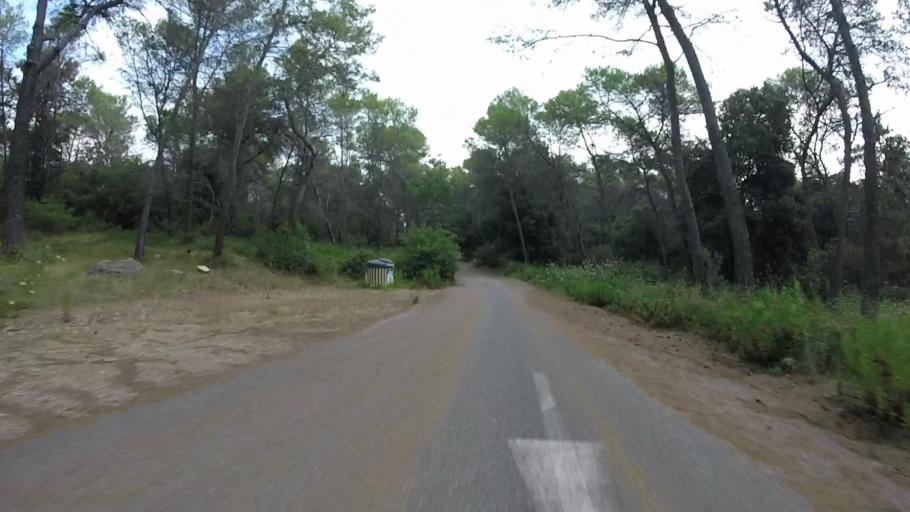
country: FR
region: Provence-Alpes-Cote d'Azur
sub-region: Departement des Alpes-Maritimes
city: Vallauris
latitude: 43.6106
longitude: 7.0432
